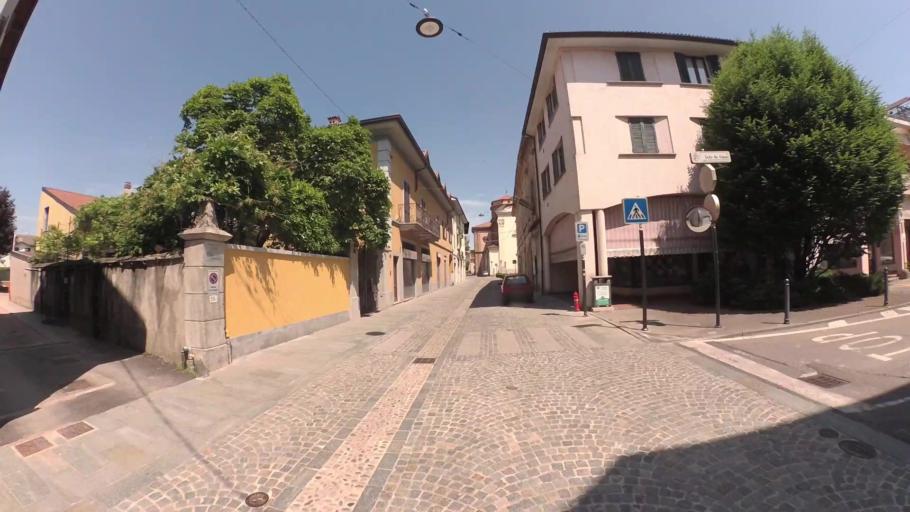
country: IT
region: Lombardy
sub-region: Provincia di Varese
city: Tradate
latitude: 45.7148
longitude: 8.9051
